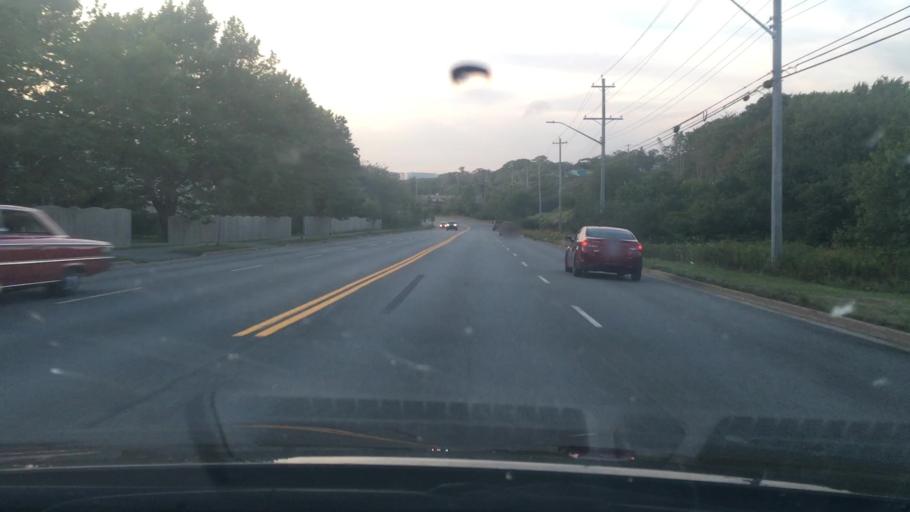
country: CA
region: Nova Scotia
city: Halifax
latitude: 44.6323
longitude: -63.5220
